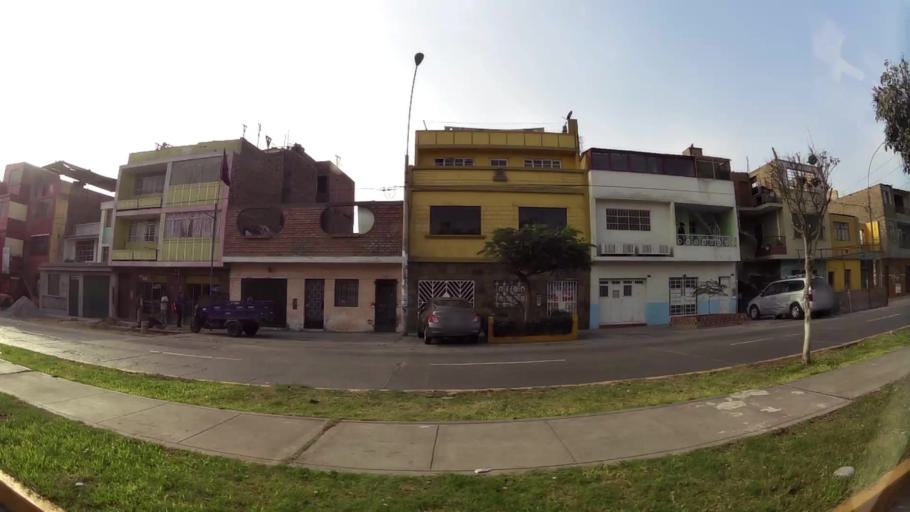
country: PE
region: Callao
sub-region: Callao
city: Callao
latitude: -12.0285
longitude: -77.0882
